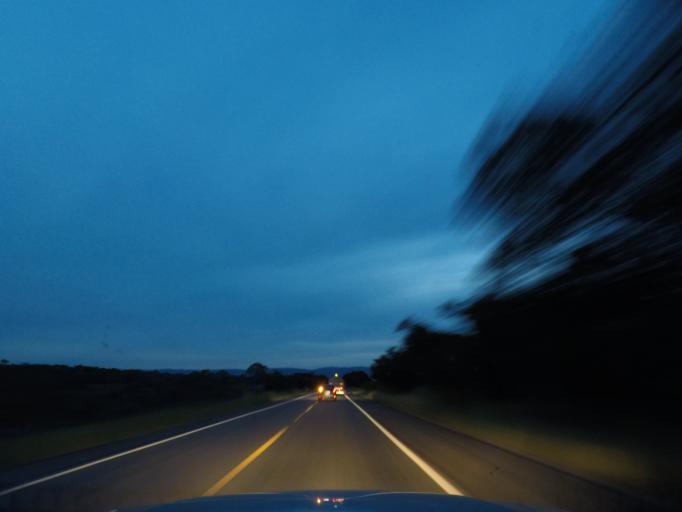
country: BR
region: Bahia
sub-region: Andarai
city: Vera Cruz
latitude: -12.4950
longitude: -41.3116
